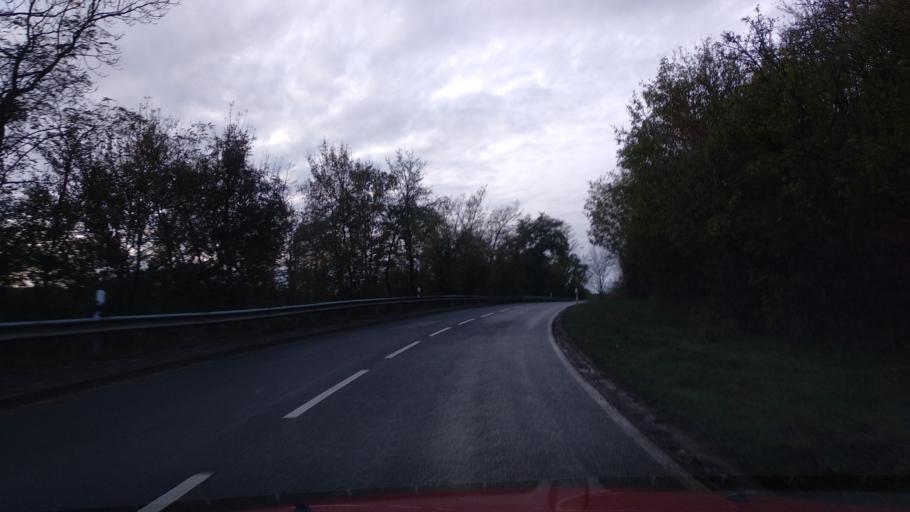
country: DE
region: North Rhine-Westphalia
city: Brakel
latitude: 51.6912
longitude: 9.2232
